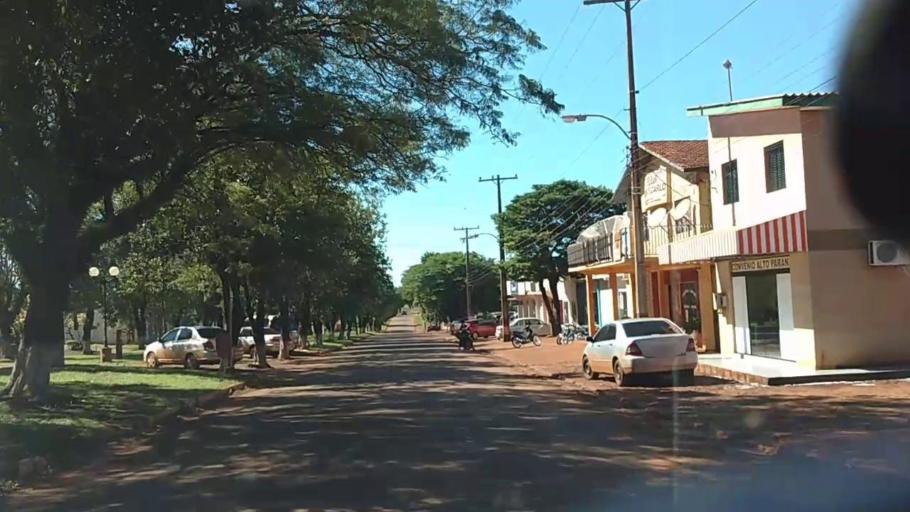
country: PY
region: Alto Parana
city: Naranjal
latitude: -25.9731
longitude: -55.1931
